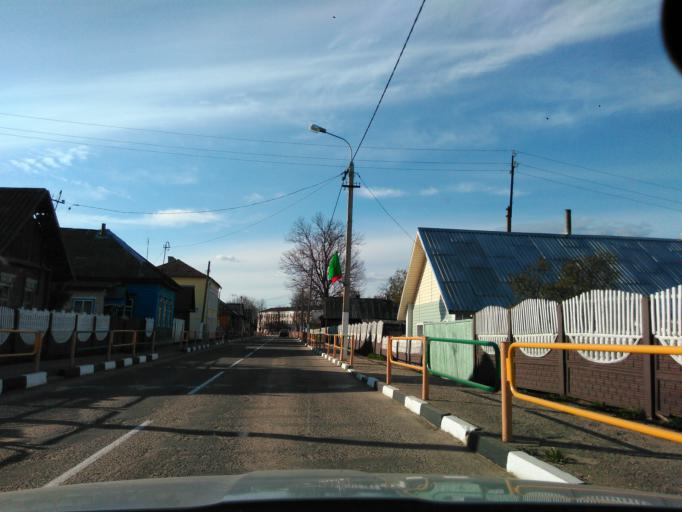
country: BY
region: Vitebsk
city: Chashniki
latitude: 54.8571
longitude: 29.1665
